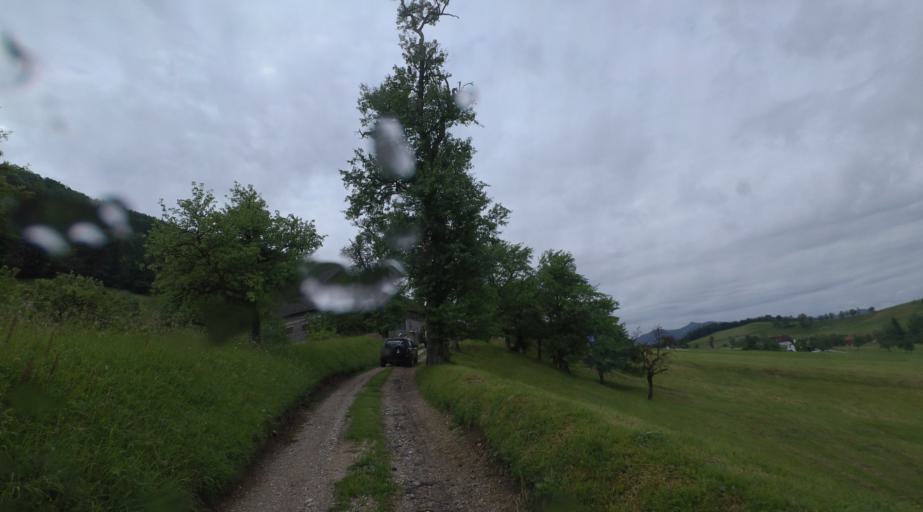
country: AT
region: Upper Austria
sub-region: Politischer Bezirk Kirchdorf an der Krems
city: Micheldorf in Oberoesterreich
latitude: 47.8965
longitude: 14.1690
